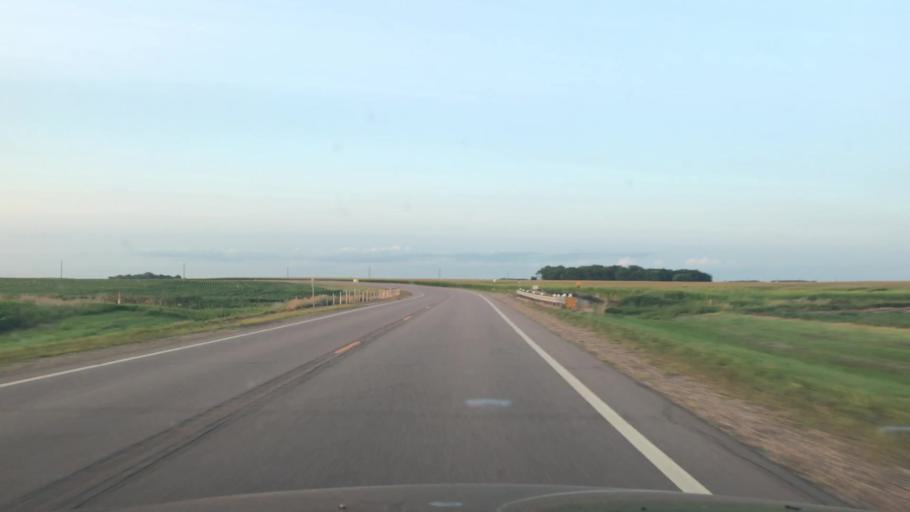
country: US
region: Minnesota
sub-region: Redwood County
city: Redwood Falls
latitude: 44.4179
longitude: -95.1207
